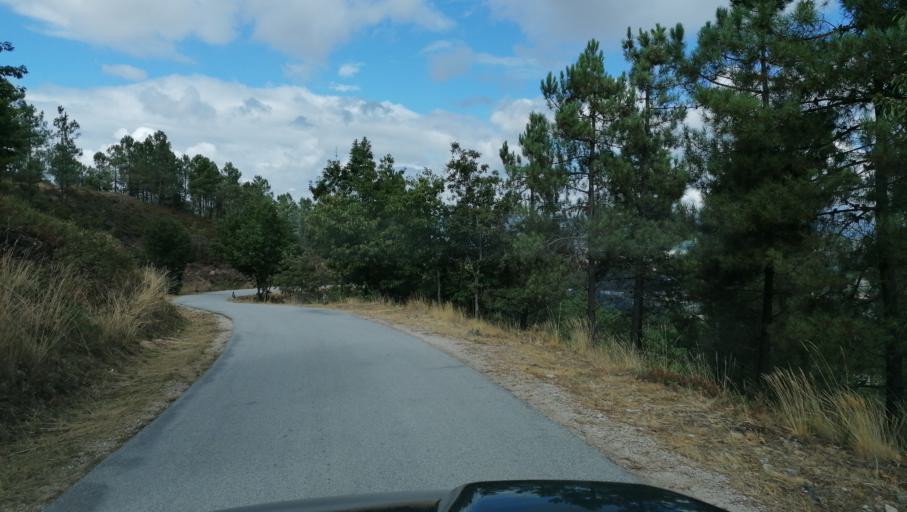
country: PT
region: Vila Real
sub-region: Vila Pouca de Aguiar
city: Vila Pouca de Aguiar
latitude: 41.5306
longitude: -7.5929
